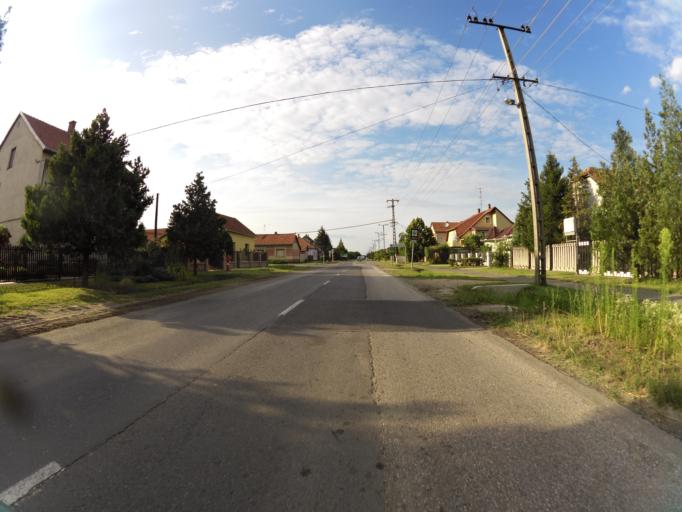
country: HU
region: Csongrad
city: Sandorfalva
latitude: 46.3679
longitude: 20.1143
